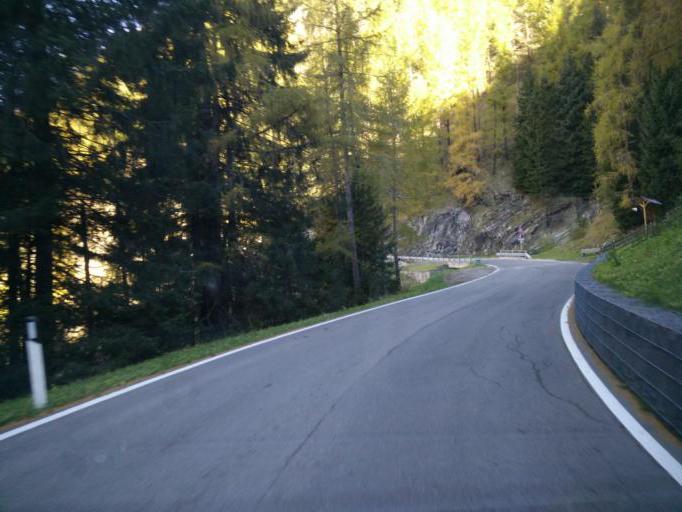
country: IT
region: Trentino-Alto Adige
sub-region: Bolzano
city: Moso in Passiria
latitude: 46.8578
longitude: 11.1618
